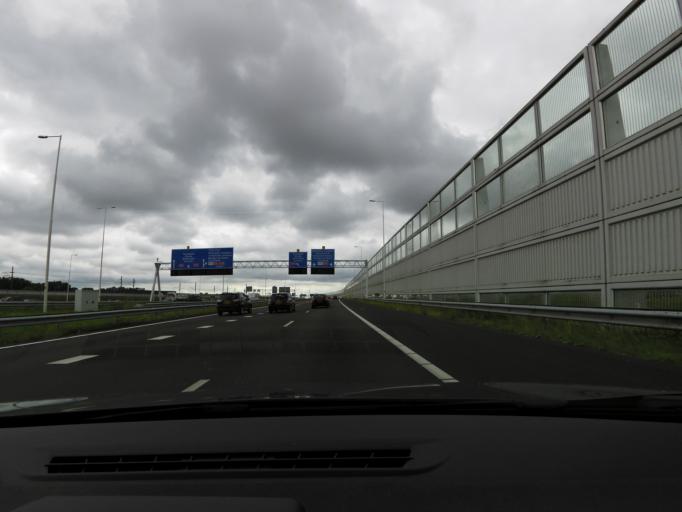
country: NL
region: South Holland
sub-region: Gemeente Binnenmaas
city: Heinenoord
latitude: 51.8615
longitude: 4.4696
